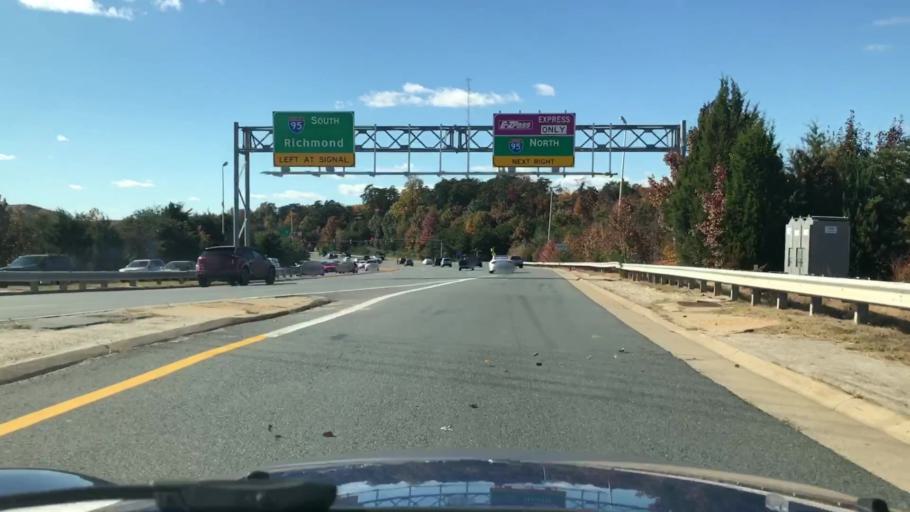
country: US
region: Virginia
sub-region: Prince William County
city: Potomac Mills
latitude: 38.6570
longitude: -77.2813
